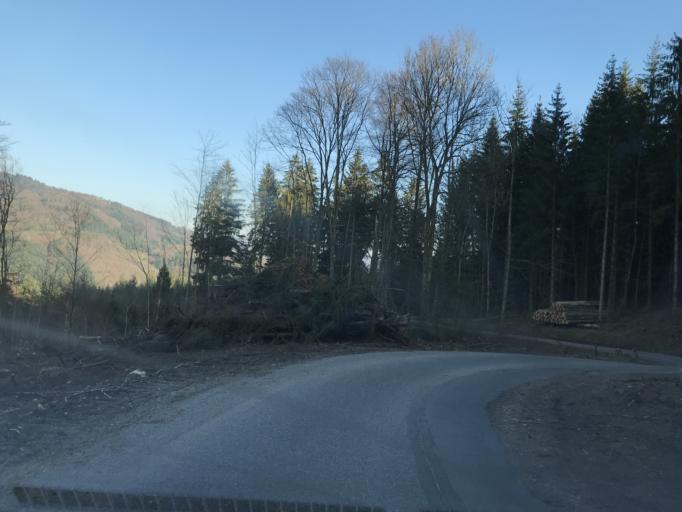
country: DE
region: Baden-Wuerttemberg
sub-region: Freiburg Region
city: Hausen
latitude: 47.6931
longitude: 7.8295
